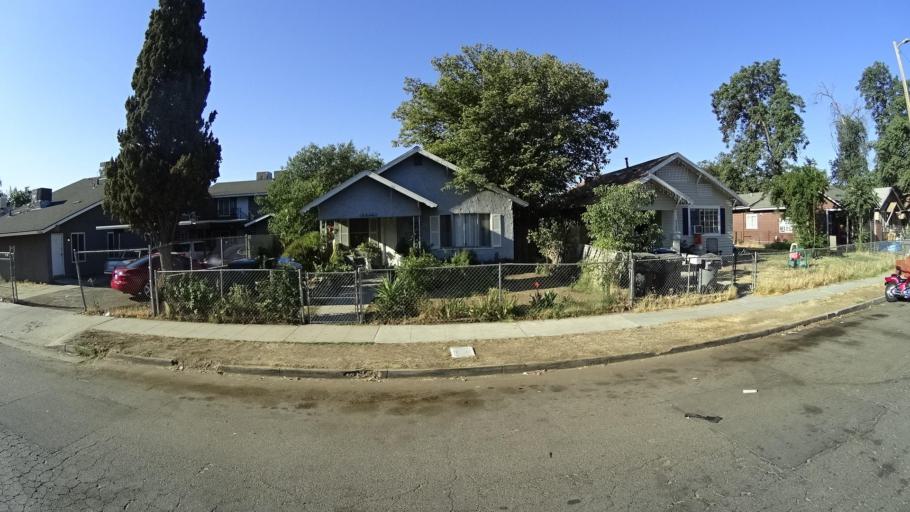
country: US
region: California
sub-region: Fresno County
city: Fresno
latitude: 36.7515
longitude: -119.7844
